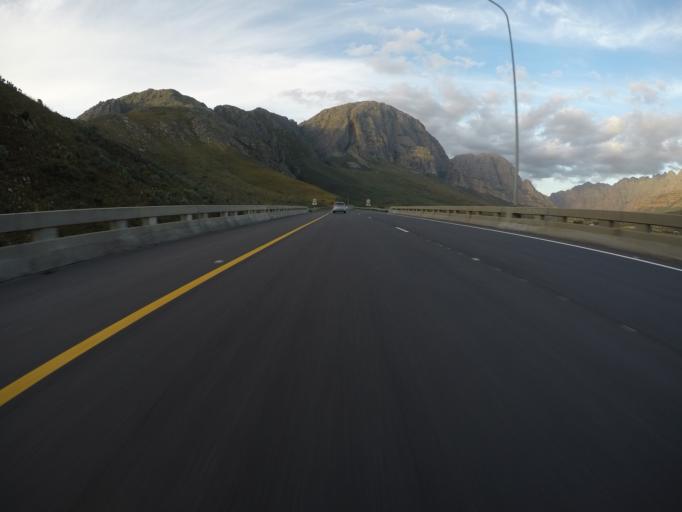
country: ZA
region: Western Cape
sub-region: Cape Winelands District Municipality
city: Paarl
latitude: -33.7306
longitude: 19.1177
